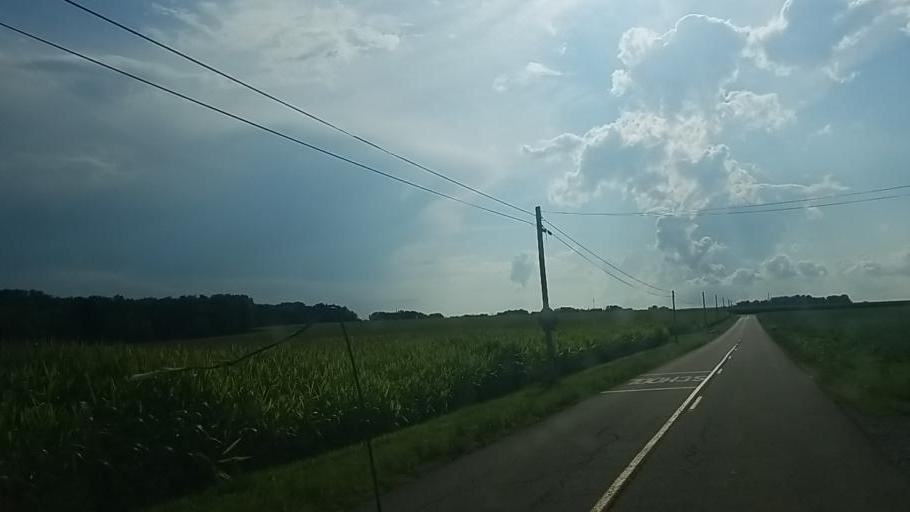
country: US
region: Ohio
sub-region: Wayne County
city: Smithville
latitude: 40.8658
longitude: -81.8737
